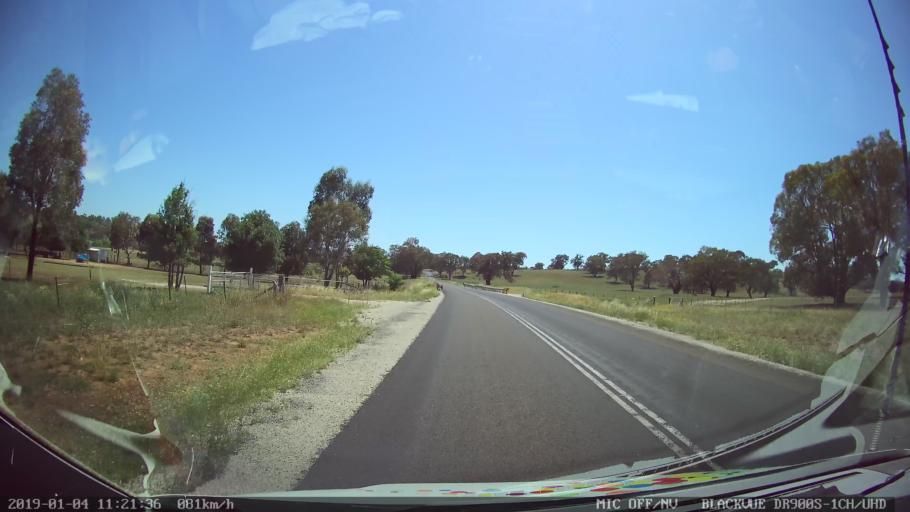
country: AU
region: New South Wales
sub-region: Cabonne
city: Molong
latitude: -33.1536
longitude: 148.7131
